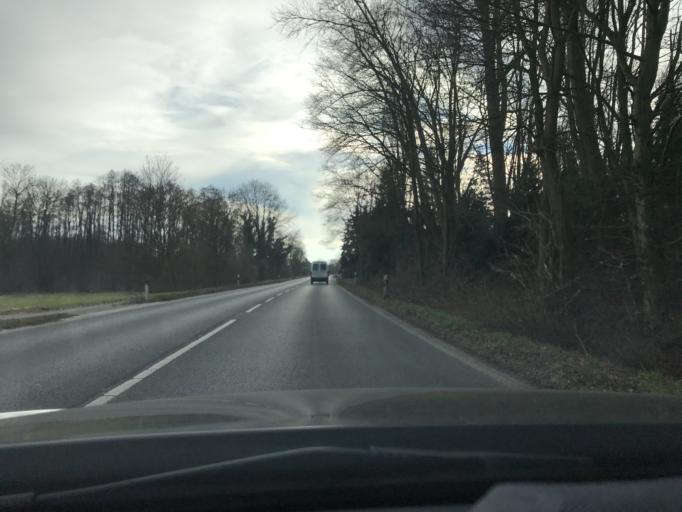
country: DE
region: North Rhine-Westphalia
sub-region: Regierungsbezirk Dusseldorf
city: Rheurdt
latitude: 51.4018
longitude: 6.4988
